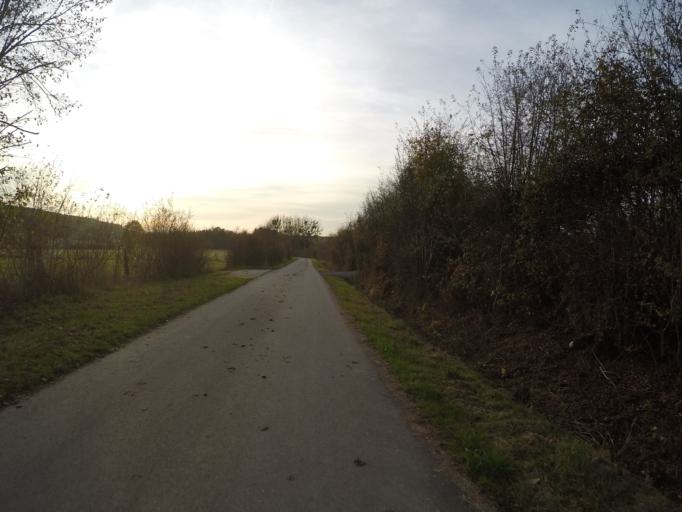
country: BE
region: Wallonia
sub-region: Province du Luxembourg
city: Hotton
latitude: 50.2625
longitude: 5.4328
